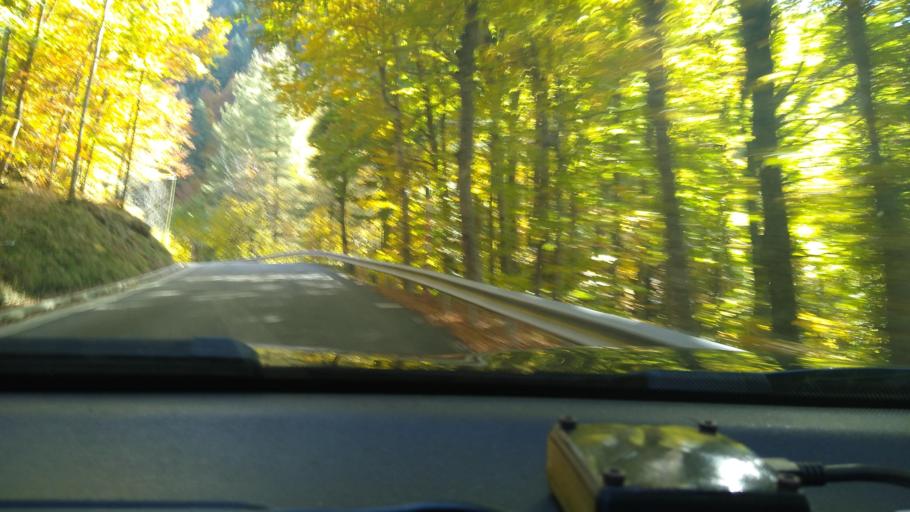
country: FR
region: Midi-Pyrenees
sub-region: Departement de l'Ariege
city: Ax-les-Thermes
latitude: 42.7200
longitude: 1.9068
